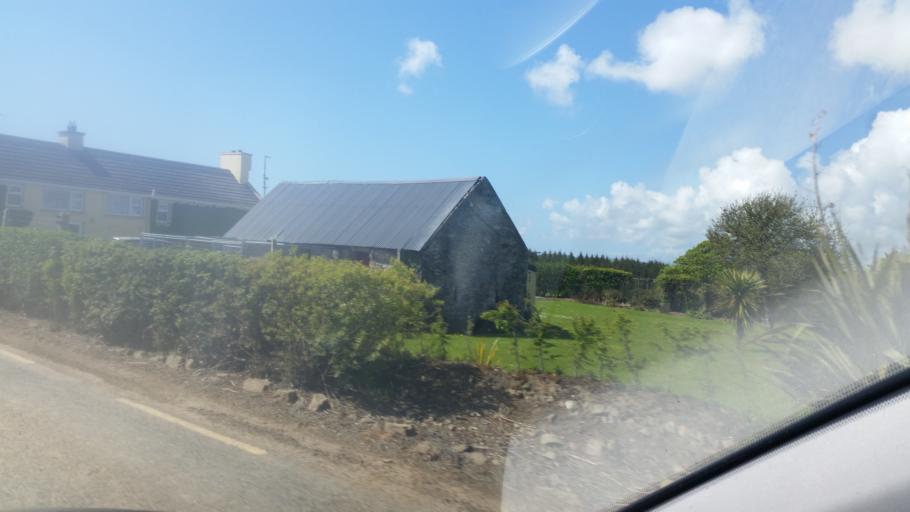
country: IE
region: Munster
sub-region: Waterford
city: Dunmore East
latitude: 52.2224
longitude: -6.8620
